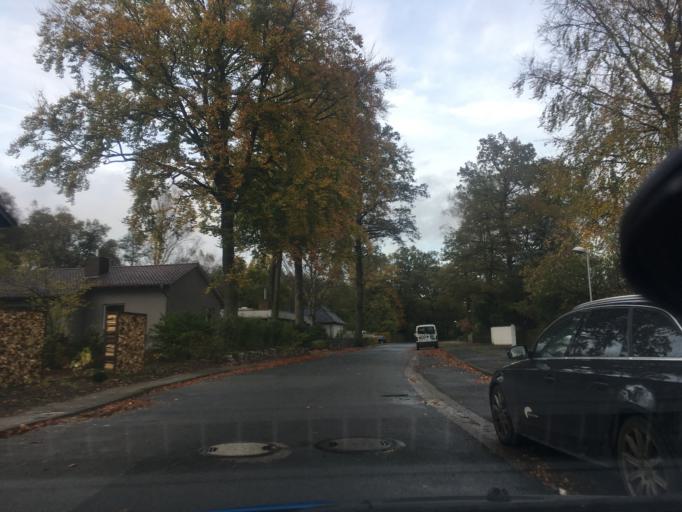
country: DE
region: Lower Saxony
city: Lueneburg
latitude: 53.2325
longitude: 10.4164
